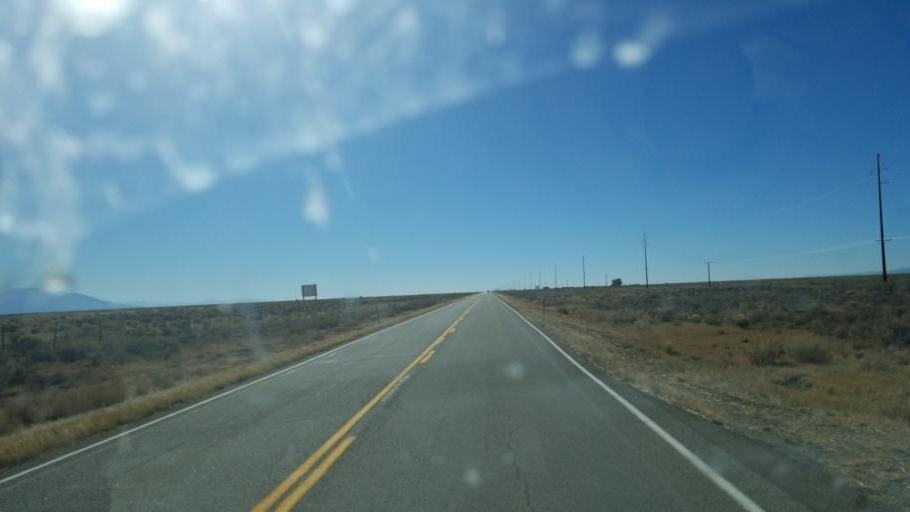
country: US
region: Colorado
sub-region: Saguache County
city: Saguache
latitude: 37.9898
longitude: -105.9075
